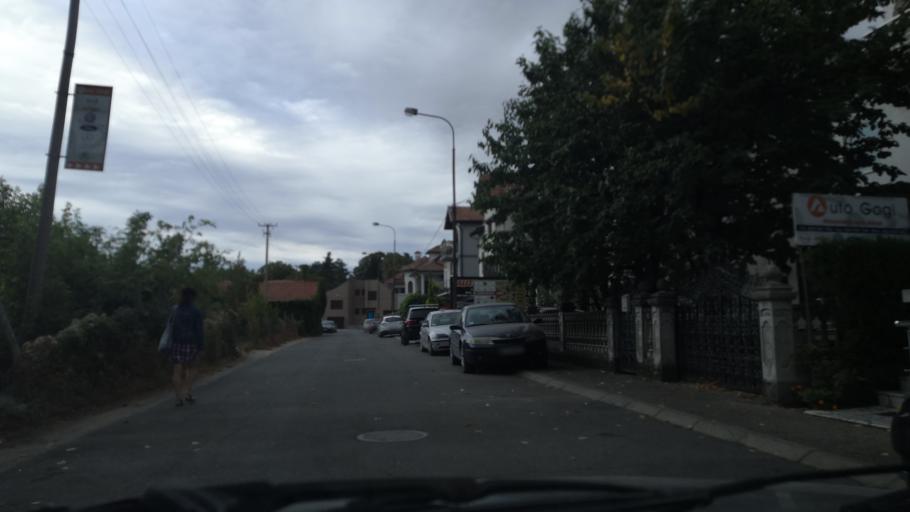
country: RS
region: Central Serbia
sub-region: Borski Okrug
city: Negotin
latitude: 44.2295
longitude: 22.5253
